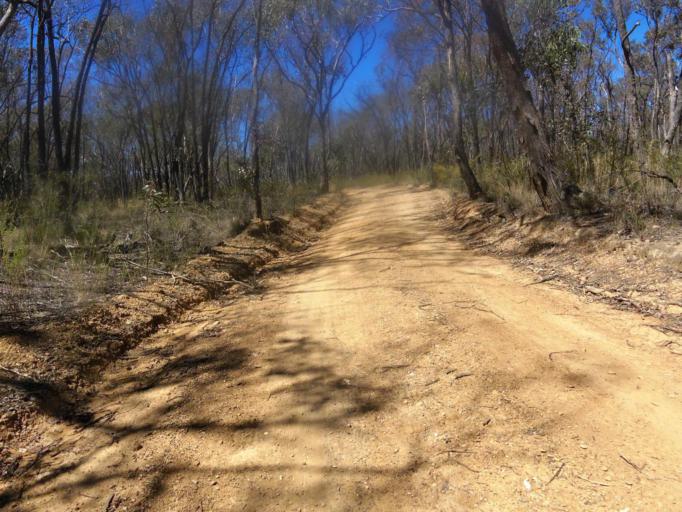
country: AU
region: Victoria
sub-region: Mount Alexander
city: Castlemaine
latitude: -36.9974
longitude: 144.1049
